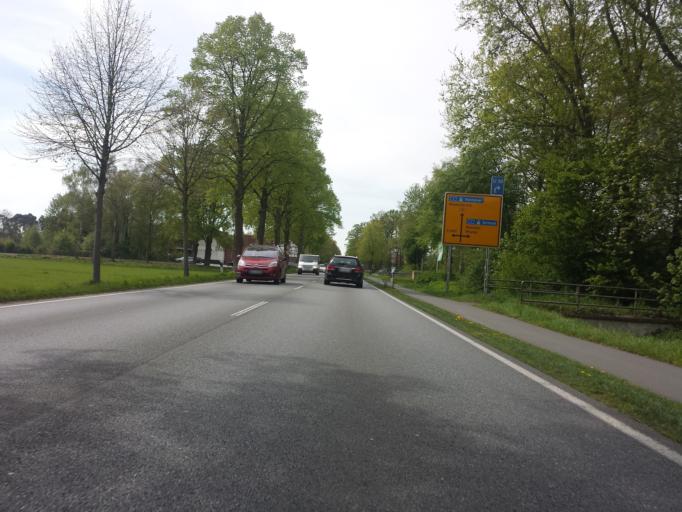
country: DE
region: North Rhine-Westphalia
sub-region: Regierungsbezirk Detmold
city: Rheda-Wiedenbruck
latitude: 51.8664
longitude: 8.3405
